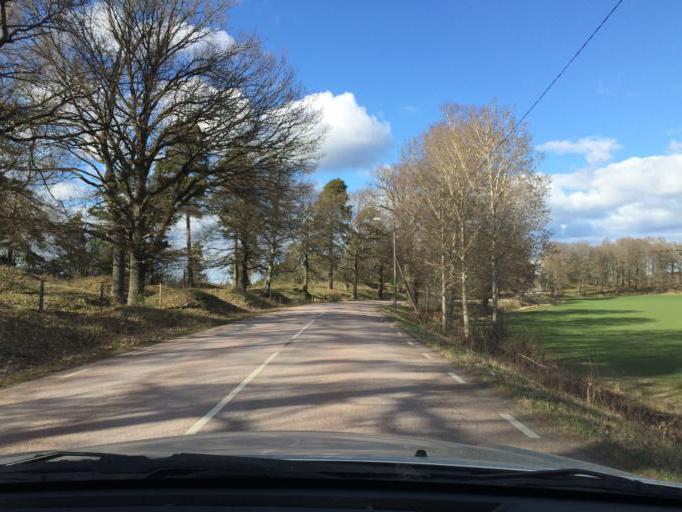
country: SE
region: Soedermanland
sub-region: Eskilstuna Kommun
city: Kvicksund
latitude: 59.4368
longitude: 16.3379
